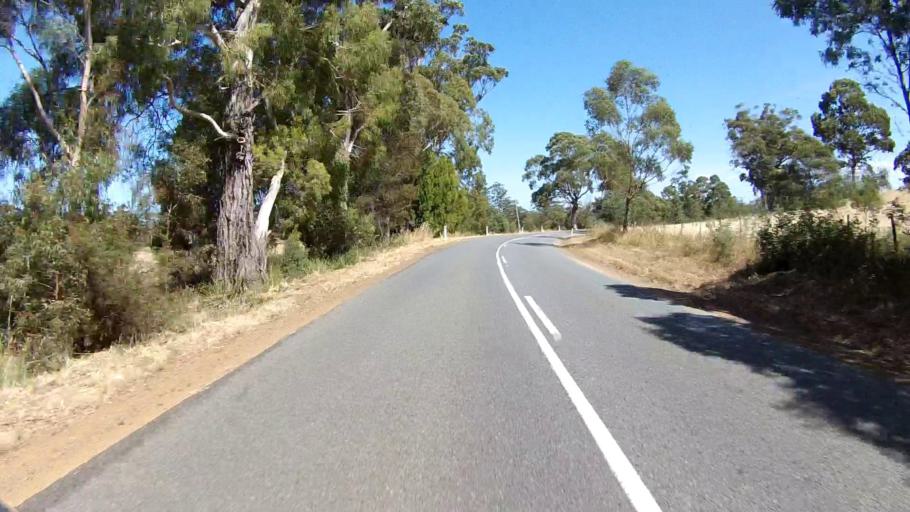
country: AU
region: Tasmania
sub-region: Sorell
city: Sorell
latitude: -42.3152
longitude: 147.9603
